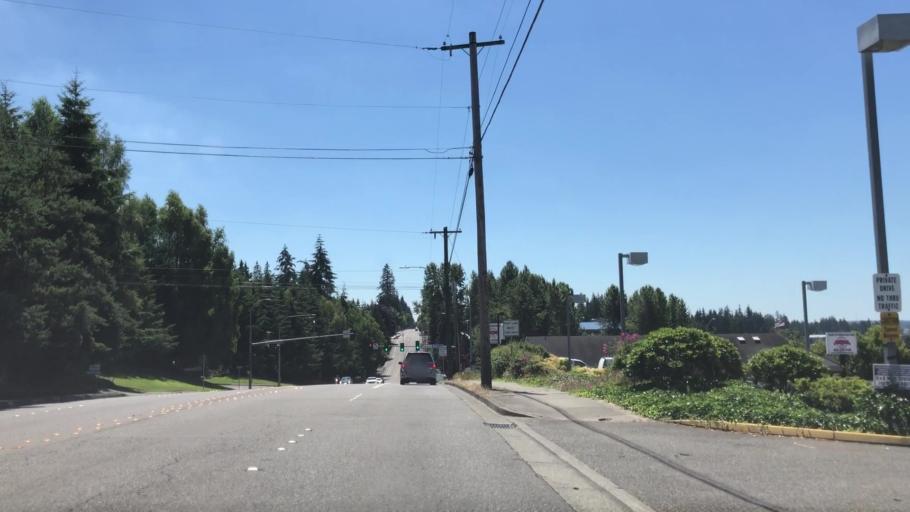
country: US
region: Washington
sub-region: Snohomish County
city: Alderwood Manor
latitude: 47.8477
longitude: -122.2926
